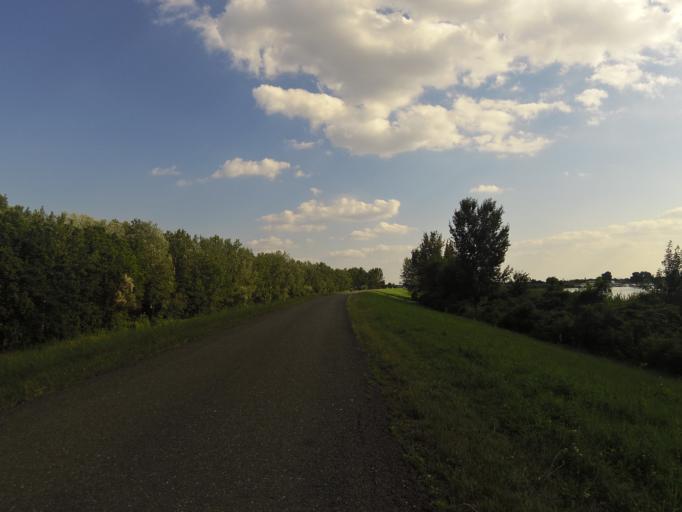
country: HU
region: Jasz-Nagykun-Szolnok
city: Abadszalok
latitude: 47.4926
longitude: 20.6086
